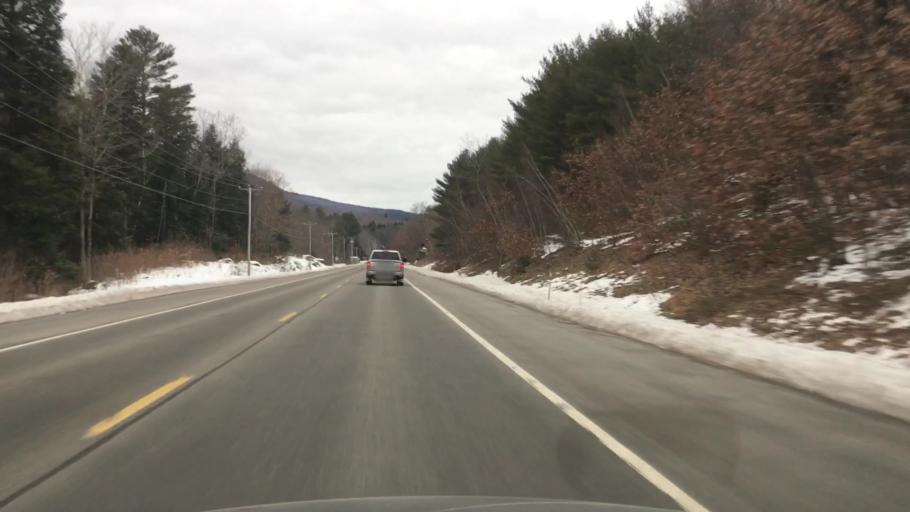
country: US
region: New Hampshire
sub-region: Merrimack County
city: Newbury
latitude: 43.3009
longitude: -72.0039
